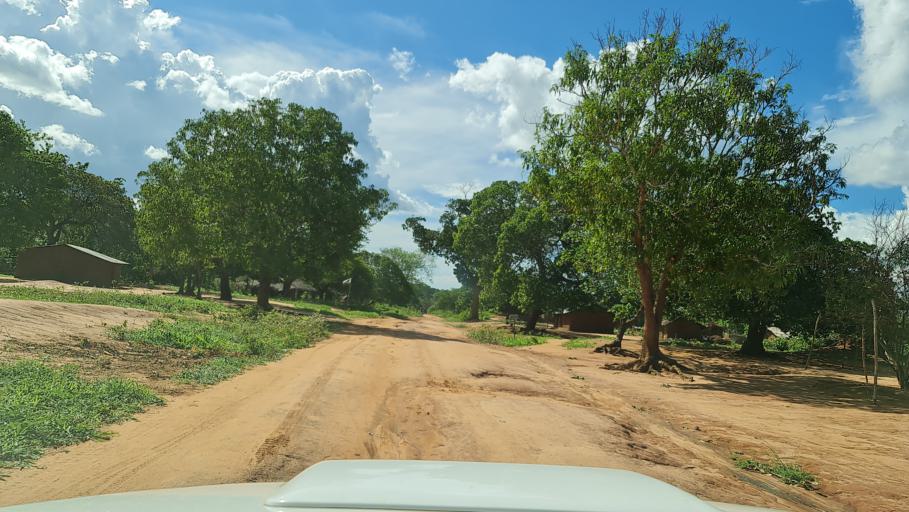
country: MZ
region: Nampula
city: Ilha de Mocambique
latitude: -15.4188
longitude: 40.2637
